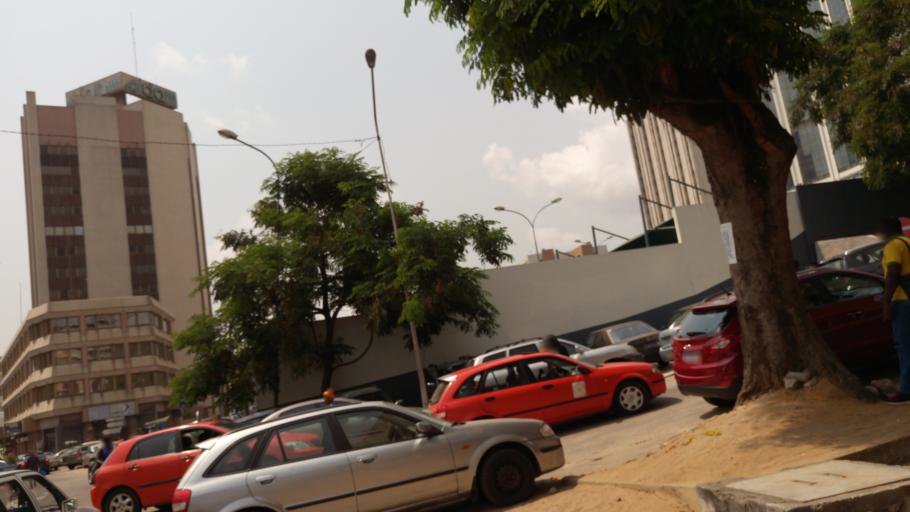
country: CI
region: Lagunes
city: Abidjan
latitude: 5.3190
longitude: -4.0161
